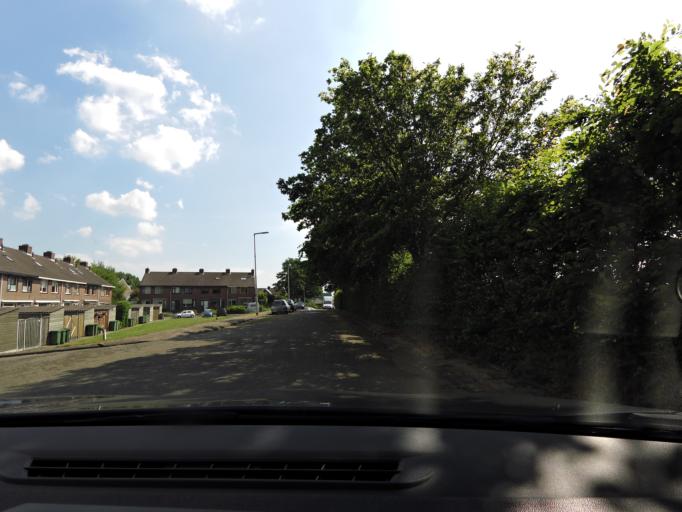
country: NL
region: South Holland
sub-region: Gemeente Schiedam
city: Schiedam
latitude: 51.8933
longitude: 4.3873
